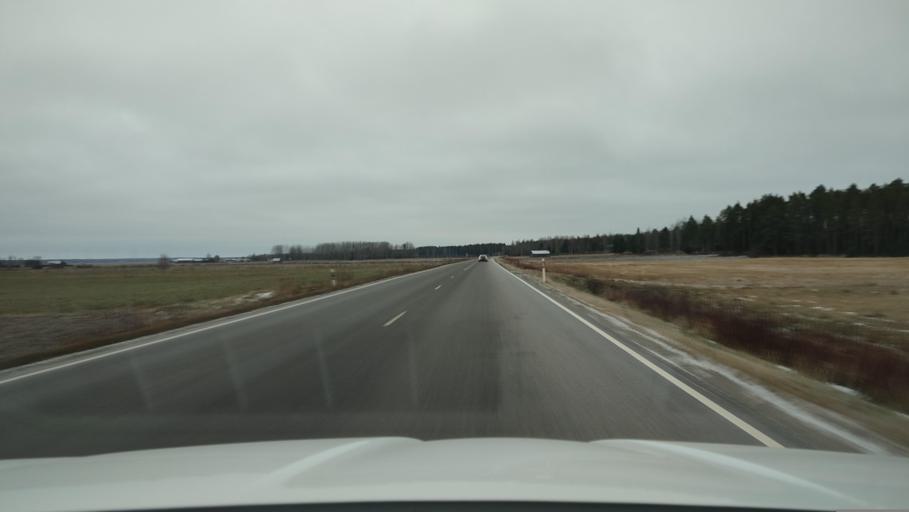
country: FI
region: Ostrobothnia
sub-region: Sydosterbotten
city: Naerpes
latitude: 62.5393
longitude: 21.4662
